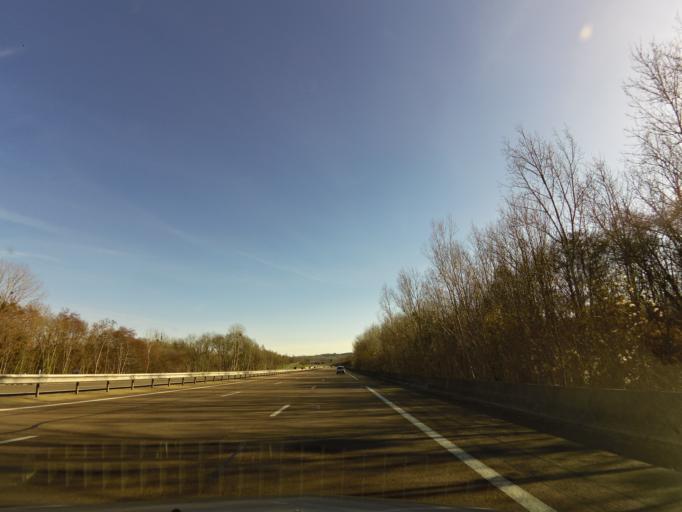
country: FR
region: Bourgogne
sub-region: Departement de l'Yonne
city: Fleury-la-Vallee
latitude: 47.8858
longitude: 3.4231
